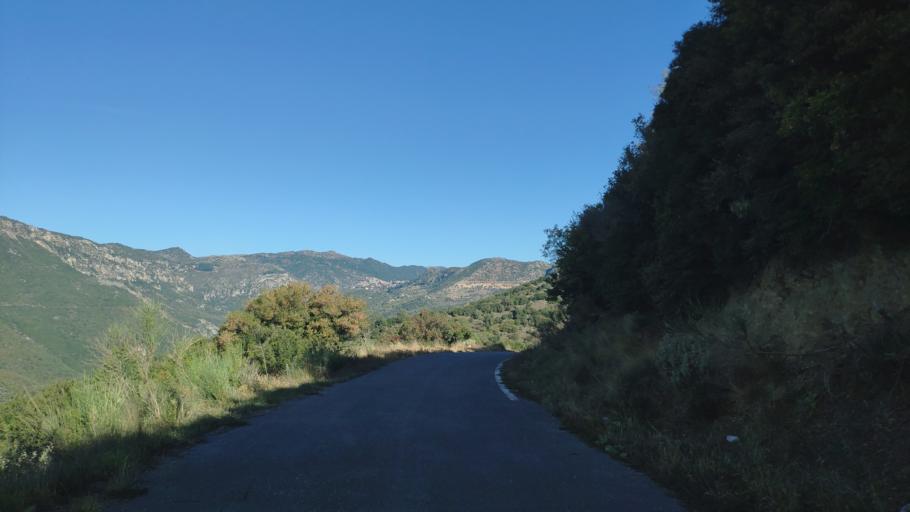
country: GR
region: Peloponnese
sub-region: Nomos Arkadias
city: Dimitsana
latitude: 37.5525
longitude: 22.0605
